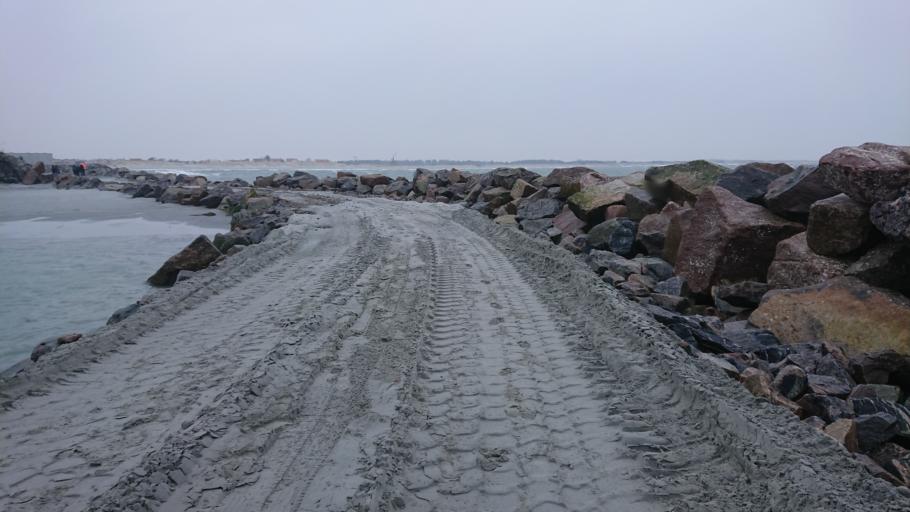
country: DK
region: North Denmark
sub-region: Frederikshavn Kommune
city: Skagen
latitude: 57.7188
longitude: 10.6092
